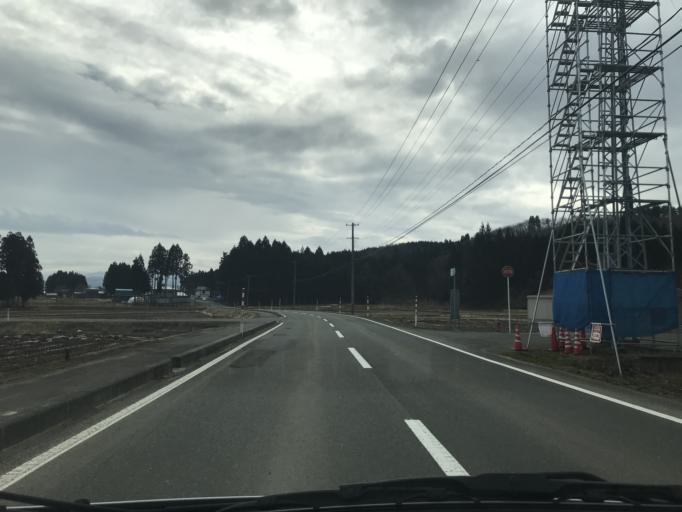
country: JP
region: Iwate
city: Hanamaki
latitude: 39.3630
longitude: 140.9928
